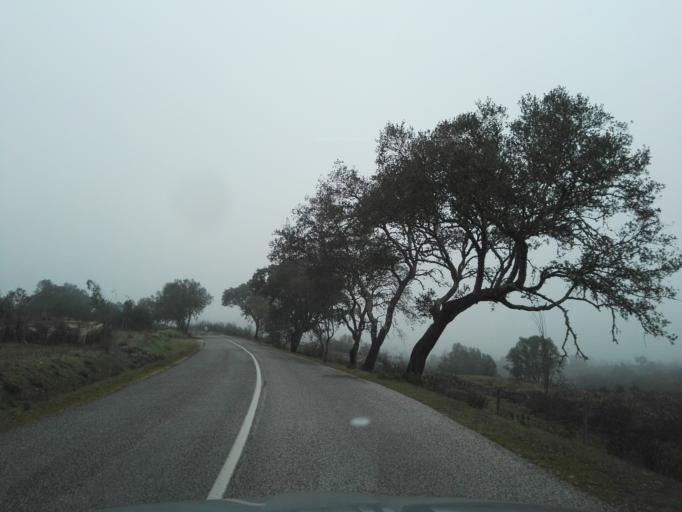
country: PT
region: Evora
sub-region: Montemor-O-Novo
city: Montemor-o-Novo
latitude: 38.7854
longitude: -8.2209
